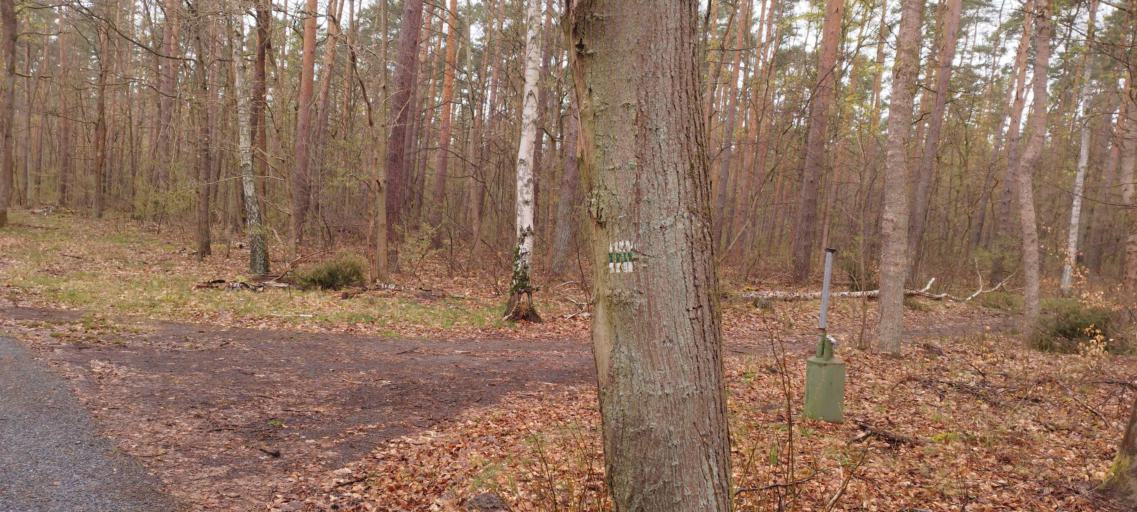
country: DE
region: Berlin
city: Rahnsdorf
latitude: 52.4593
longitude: 13.6602
